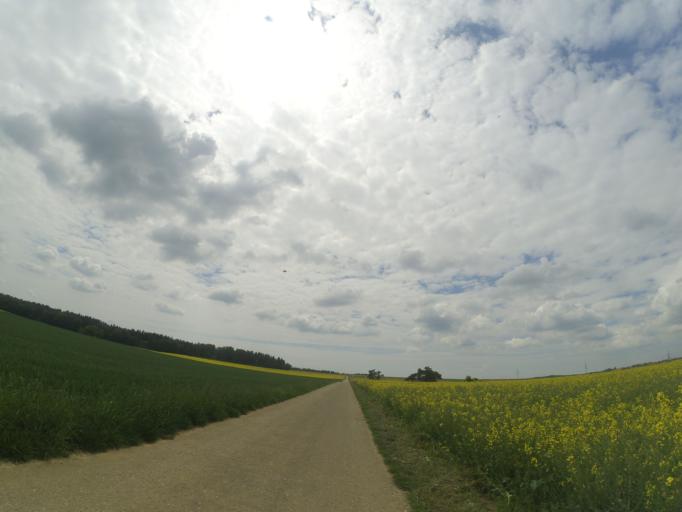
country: DE
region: Baden-Wuerttemberg
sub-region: Tuebingen Region
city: Blaubeuren
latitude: 48.4270
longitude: 9.8294
